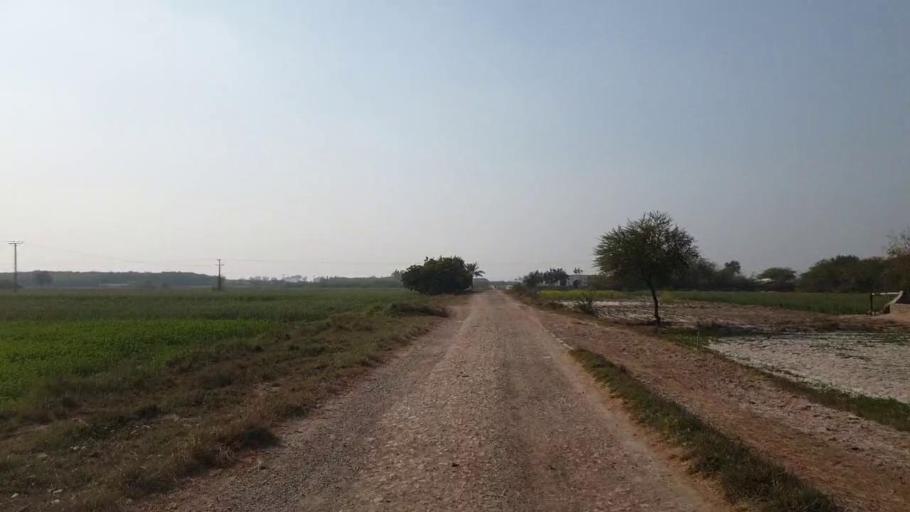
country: PK
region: Sindh
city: Tando Adam
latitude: 25.7157
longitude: 68.5665
